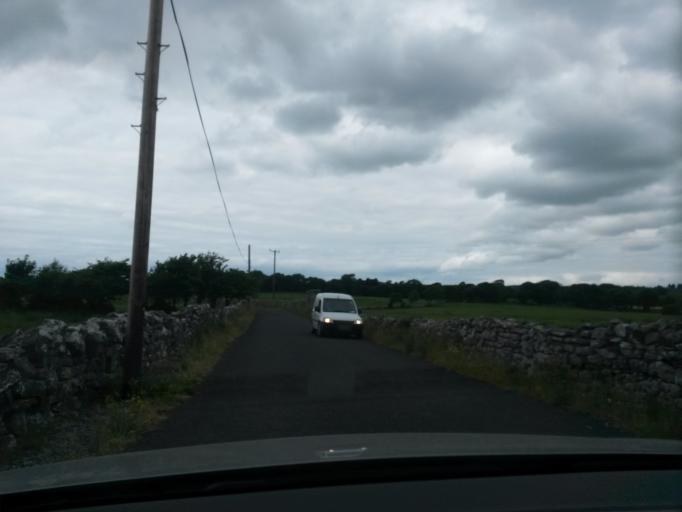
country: IE
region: Connaught
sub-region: County Galway
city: Bearna
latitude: 52.9912
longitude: -9.2205
